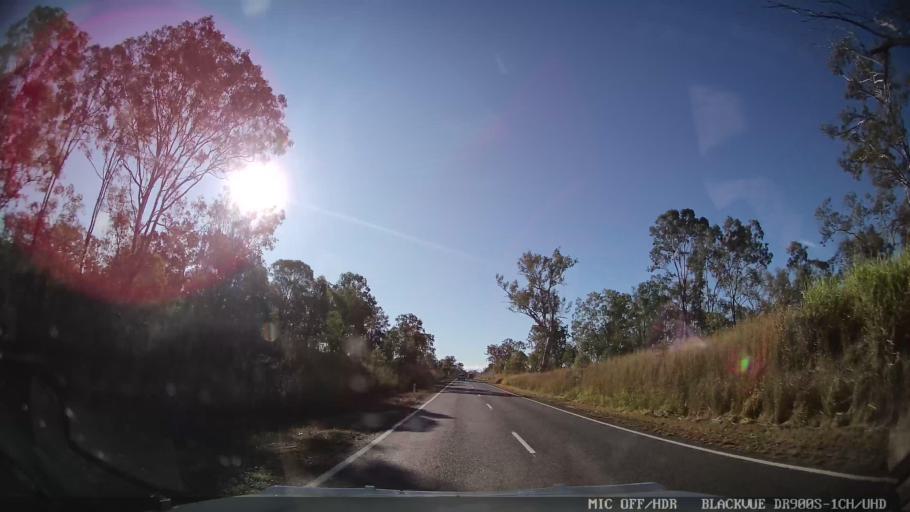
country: AU
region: Queensland
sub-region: Bundaberg
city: Sharon
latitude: -24.8272
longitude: 151.7075
